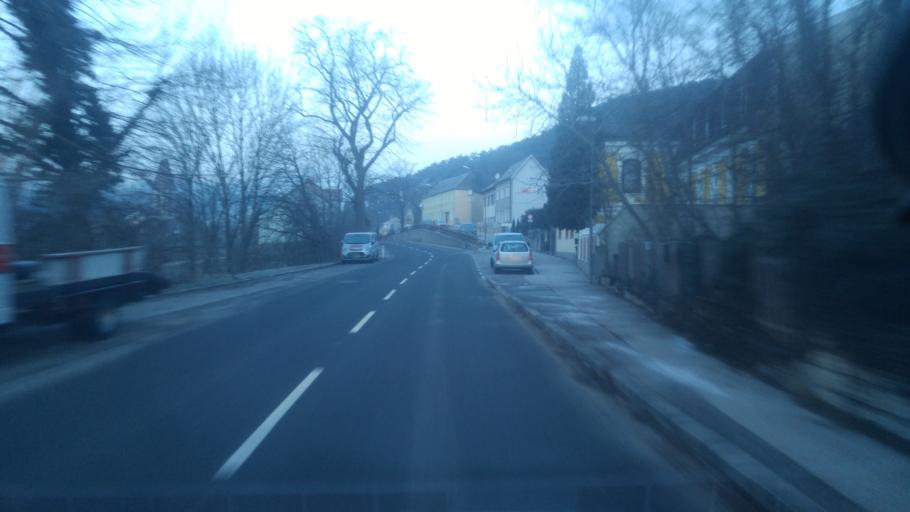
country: AT
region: Lower Austria
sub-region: Politischer Bezirk Baden
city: Pottenstein
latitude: 47.9576
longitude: 16.1006
